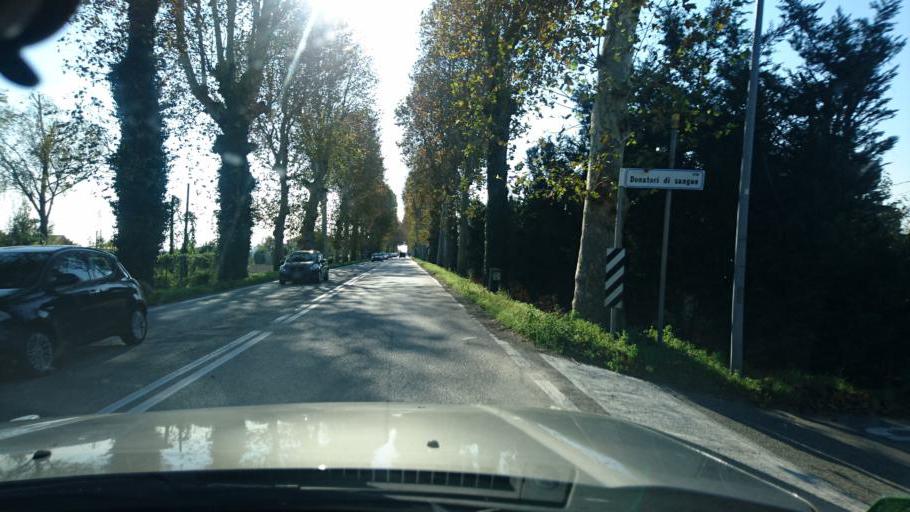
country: IT
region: Veneto
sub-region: Provincia di Padova
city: Monselice
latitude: 45.2290
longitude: 11.7549
